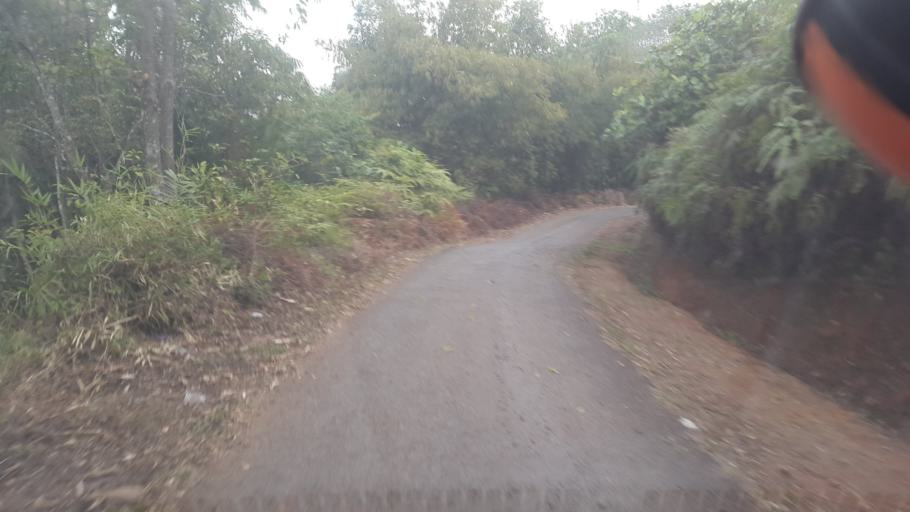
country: ID
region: West Java
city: Cigawir
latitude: -7.0764
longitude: 106.9012
